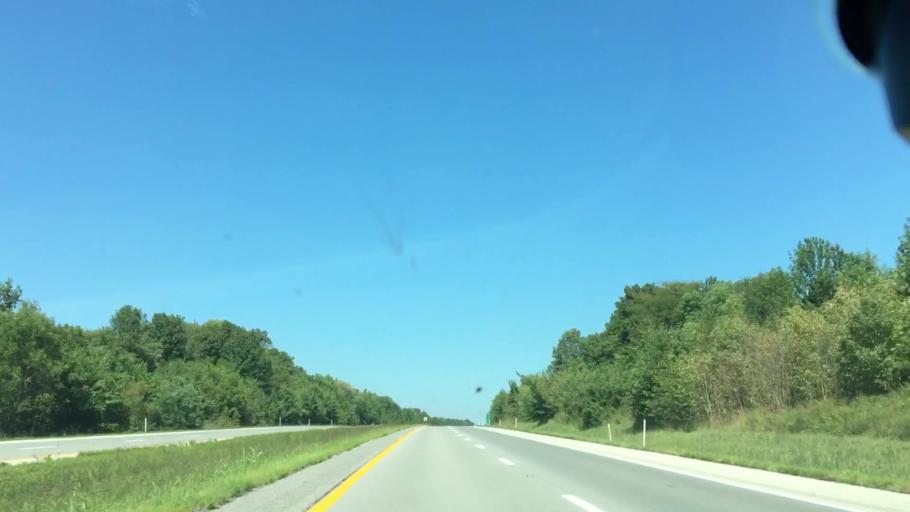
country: US
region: Kentucky
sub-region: Webster County
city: Sebree
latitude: 37.6542
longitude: -87.5127
